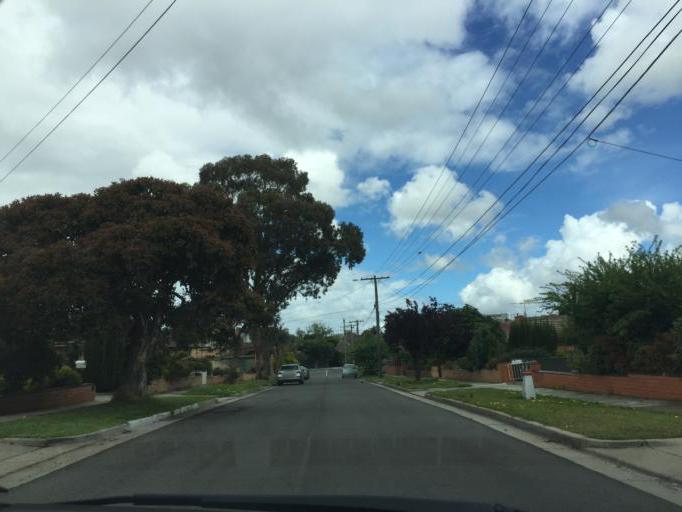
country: AU
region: Victoria
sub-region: Maribyrnong
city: Braybrook
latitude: -37.7882
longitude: 144.8399
